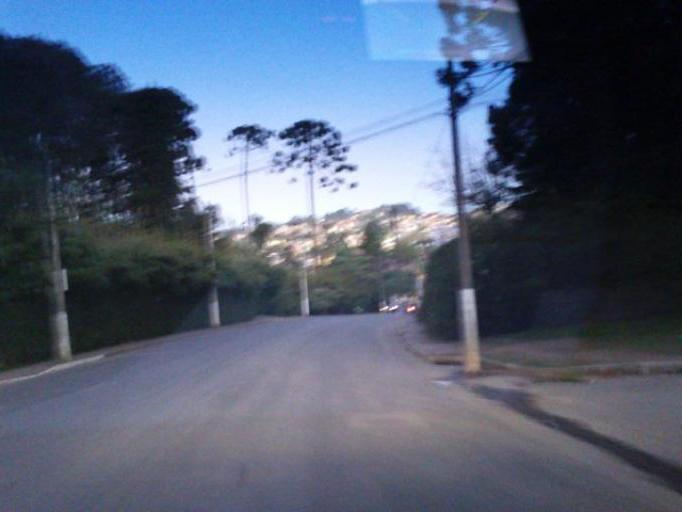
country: BR
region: Sao Paulo
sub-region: Campos Do Jordao
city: Campos do Jordao
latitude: -22.7371
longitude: -45.5949
